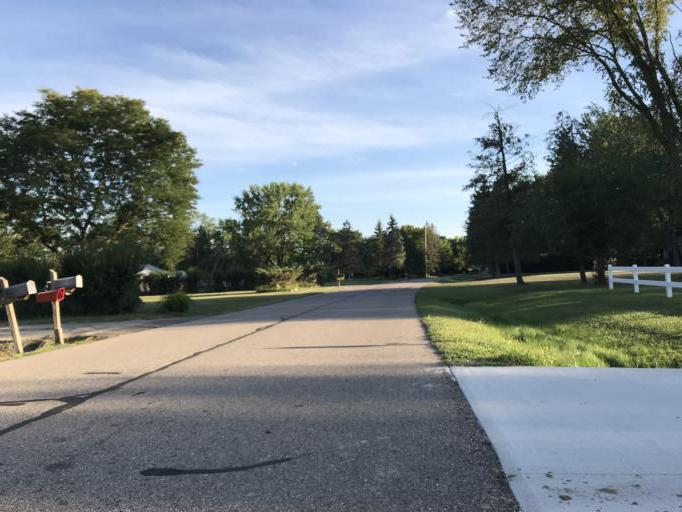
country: US
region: Michigan
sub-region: Oakland County
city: Farmington
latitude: 42.4730
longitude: -83.3487
